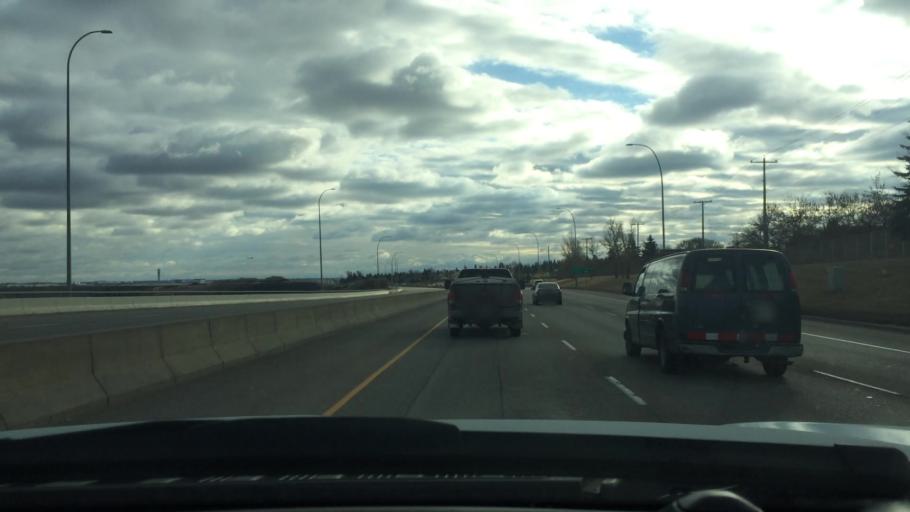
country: CA
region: Alberta
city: Calgary
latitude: 51.1359
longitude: -114.0751
